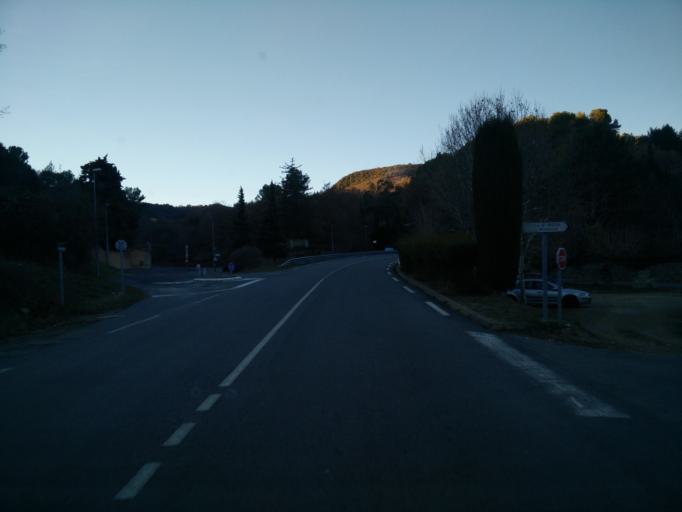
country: FR
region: Provence-Alpes-Cote d'Azur
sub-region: Departement du Var
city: Montferrat
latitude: 43.6112
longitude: 6.4801
